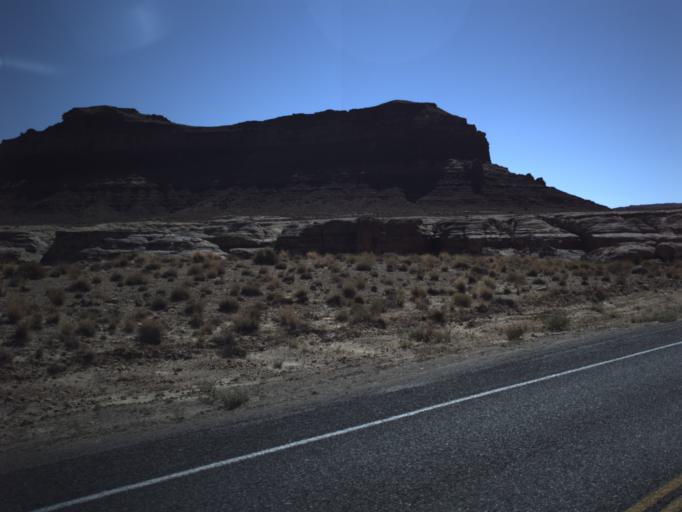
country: US
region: Utah
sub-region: San Juan County
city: Blanding
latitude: 37.9179
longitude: -110.3883
